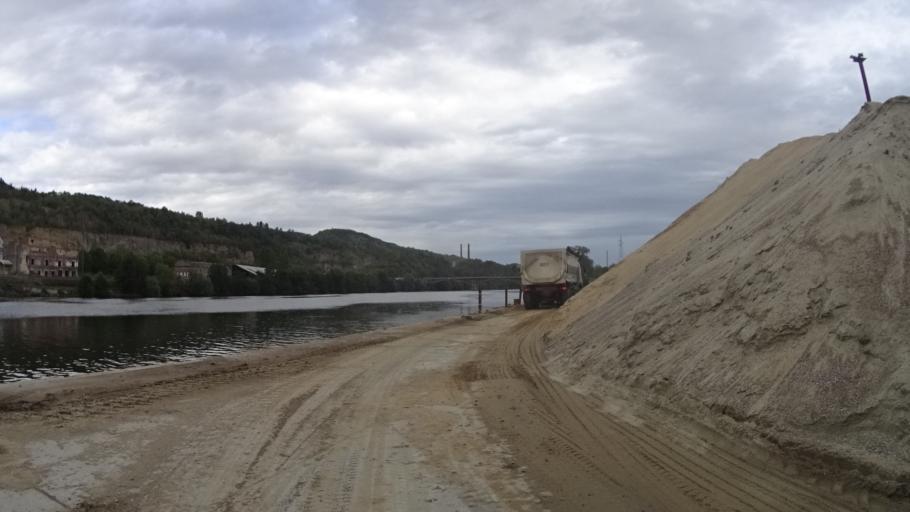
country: BE
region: Wallonia
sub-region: Province de Liege
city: Amay
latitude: 50.5608
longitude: 5.3488
